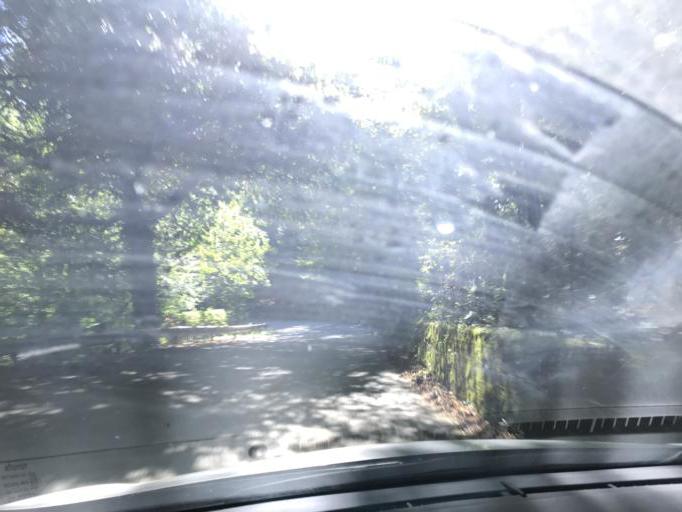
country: IT
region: Umbria
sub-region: Provincia di Terni
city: Avigliano Umbro
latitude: 42.6158
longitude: 12.4081
